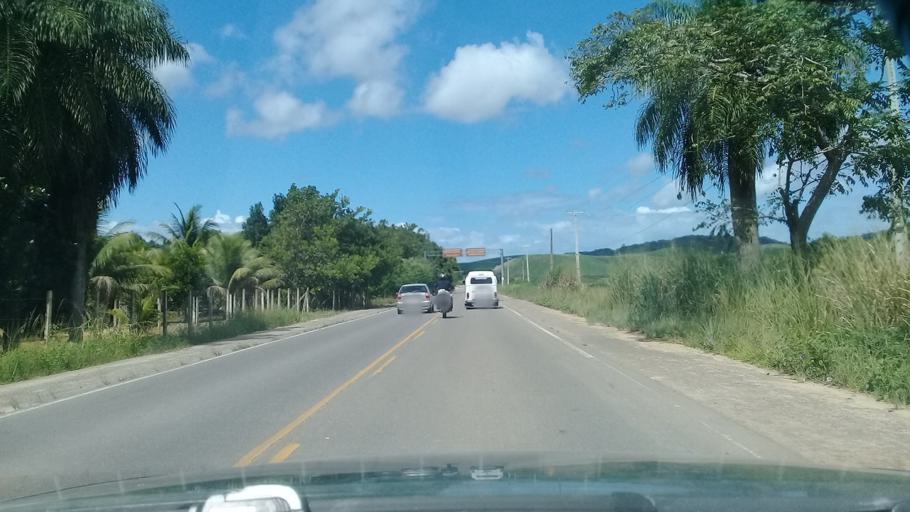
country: BR
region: Pernambuco
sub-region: Sirinhaem
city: Sirinhaem
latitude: -8.5095
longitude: -35.0956
